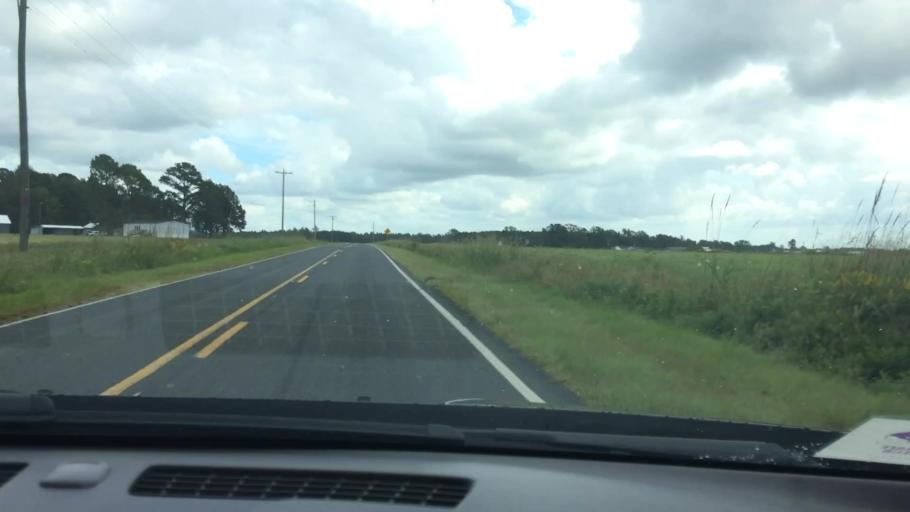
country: US
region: North Carolina
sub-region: Greene County
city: Maury
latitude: 35.5181
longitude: -77.5297
